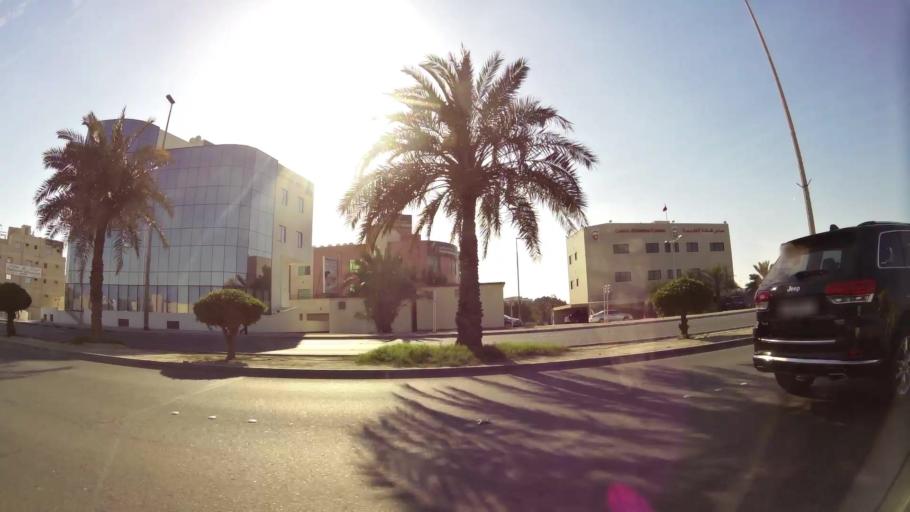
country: BH
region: Manama
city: Manama
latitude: 26.2154
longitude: 50.5653
